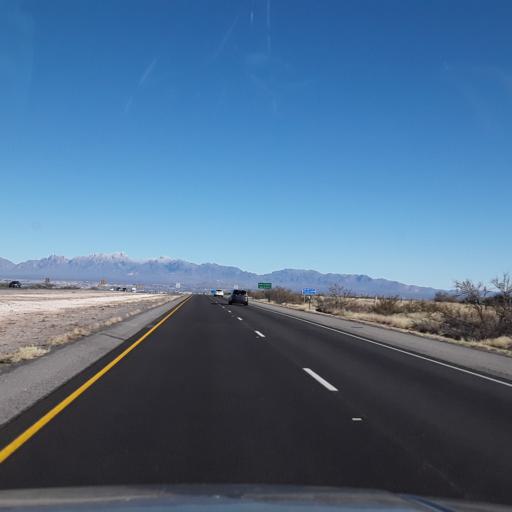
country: US
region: New Mexico
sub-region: Dona Ana County
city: Mesilla
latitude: 32.2727
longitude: -106.9150
